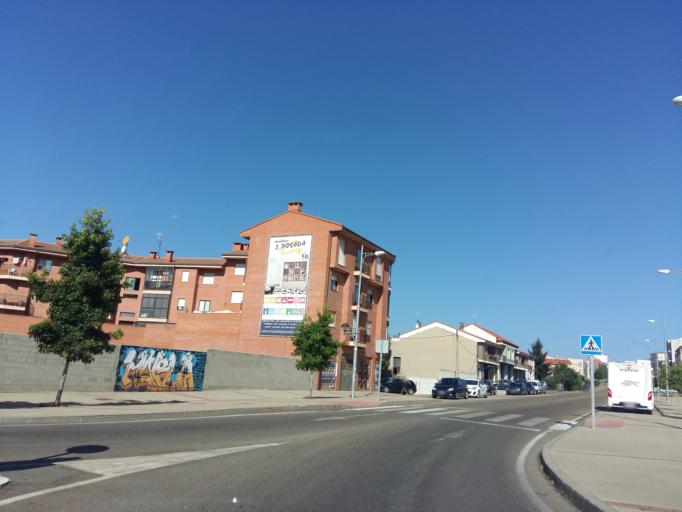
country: ES
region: Castille and Leon
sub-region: Provincia de Leon
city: Astorga
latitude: 42.4524
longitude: -6.0557
